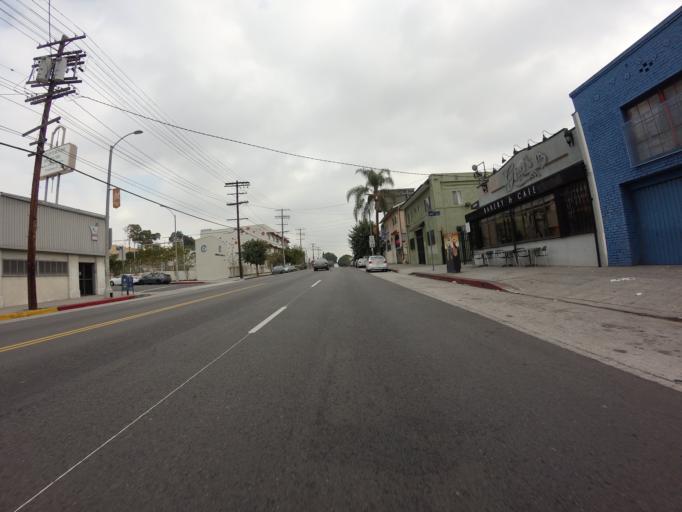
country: US
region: California
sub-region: Los Angeles County
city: Echo Park
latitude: 34.0708
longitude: -118.2696
